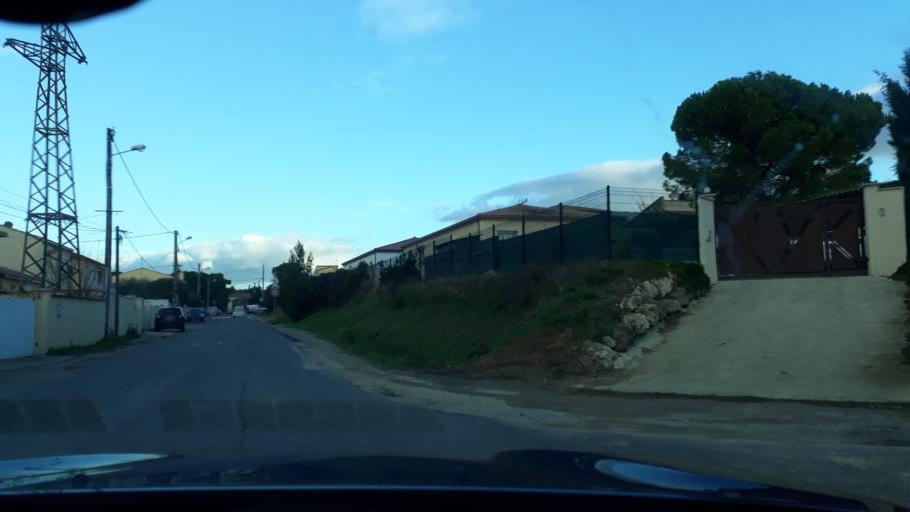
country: FR
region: Languedoc-Roussillon
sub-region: Departement de l'Herault
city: Nissan-lez-Enserune
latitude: 43.2849
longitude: 3.1332
